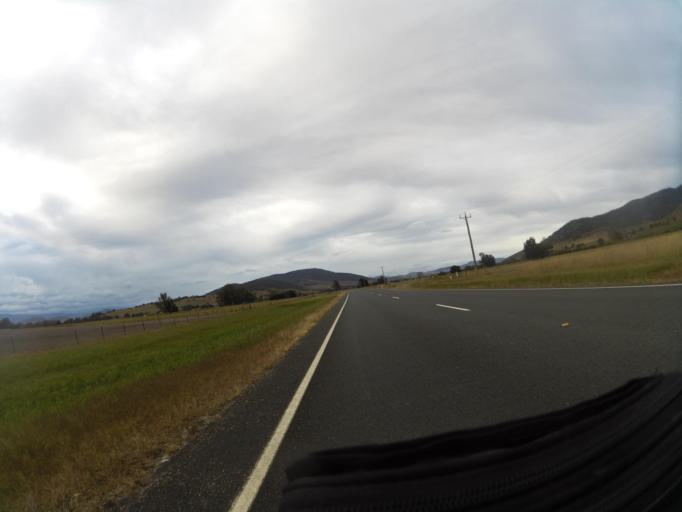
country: AU
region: New South Wales
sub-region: Snowy River
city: Jindabyne
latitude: -36.1085
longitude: 147.9798
